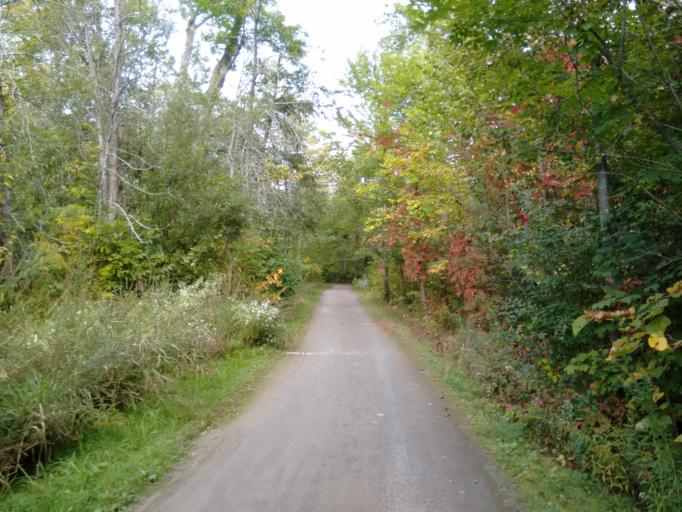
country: CA
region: Quebec
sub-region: Outaouais
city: Gatineau
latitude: 45.4723
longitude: -75.5715
